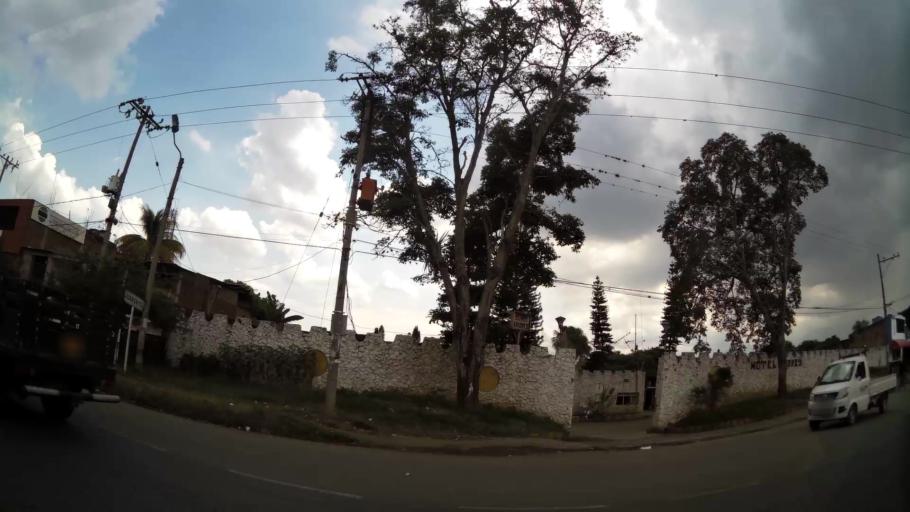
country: CO
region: Valle del Cauca
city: Cali
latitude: 3.4503
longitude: -76.4726
